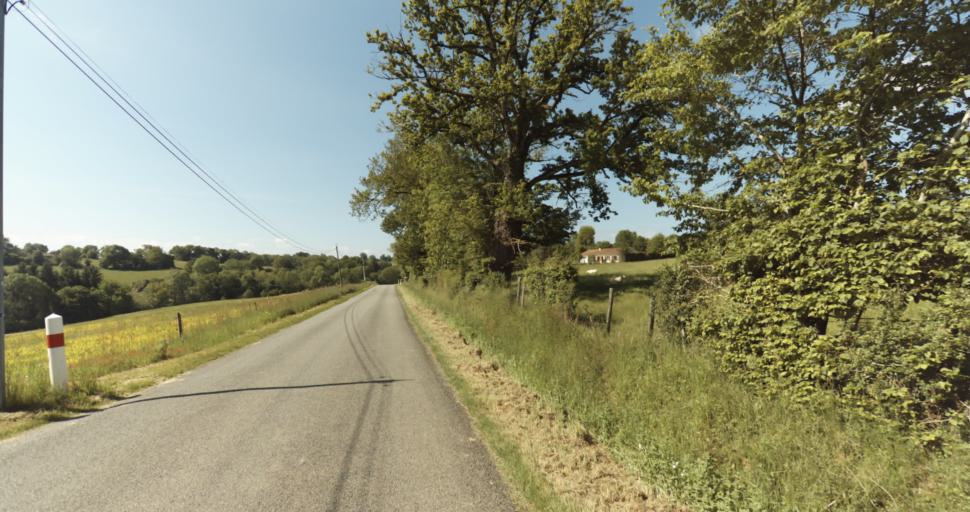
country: FR
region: Limousin
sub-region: Departement de la Haute-Vienne
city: Le Vigen
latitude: 45.7310
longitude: 1.2883
